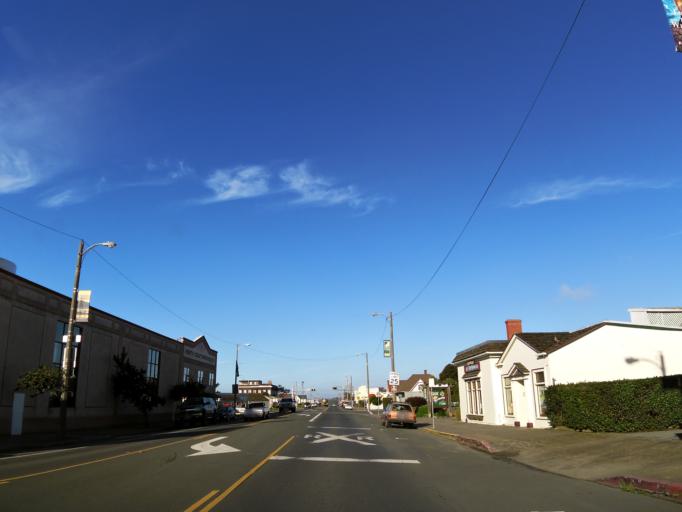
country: US
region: California
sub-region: Mendocino County
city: Fort Bragg
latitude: 39.4461
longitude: -123.8059
